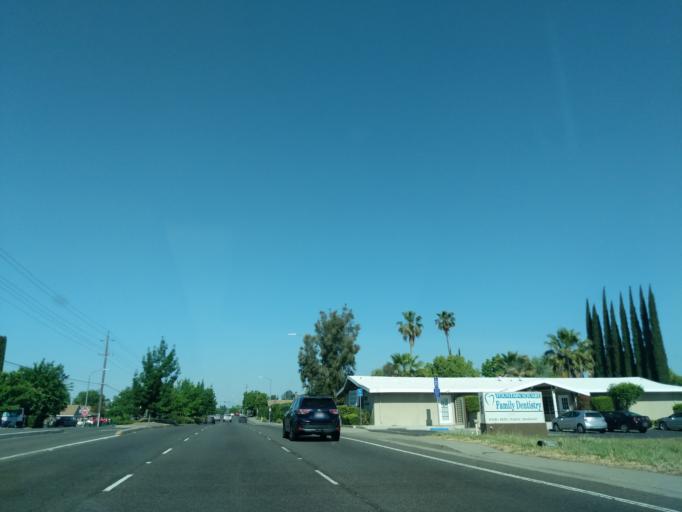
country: US
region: California
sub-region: Sacramento County
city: Citrus Heights
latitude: 38.6782
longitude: -121.3001
